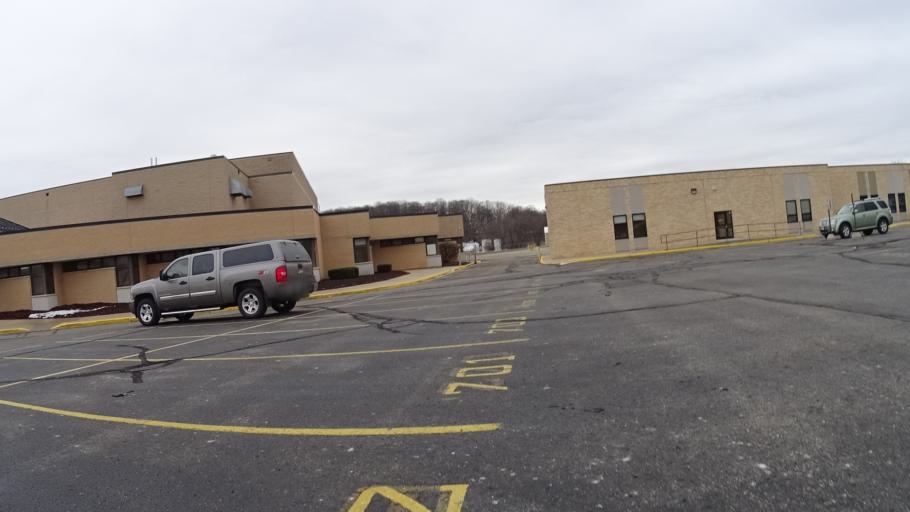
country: US
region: Wisconsin
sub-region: Washington County
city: Slinger
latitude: 43.3307
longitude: -88.2857
